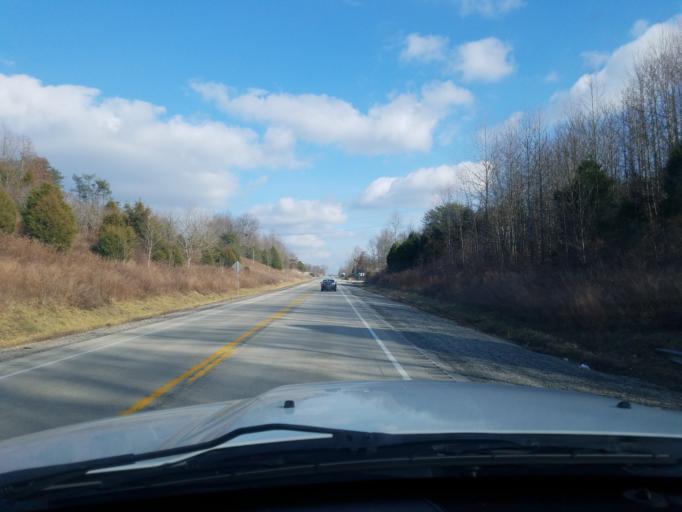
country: US
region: Kentucky
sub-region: Larue County
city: Hodgenville
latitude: 37.4686
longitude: -85.5993
